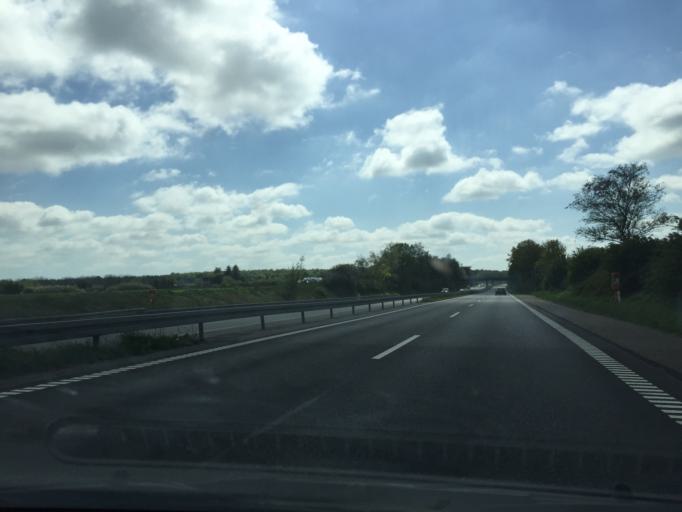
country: DK
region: Zealand
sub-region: Guldborgsund Kommune
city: Sakskobing
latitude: 54.7972
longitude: 11.6651
